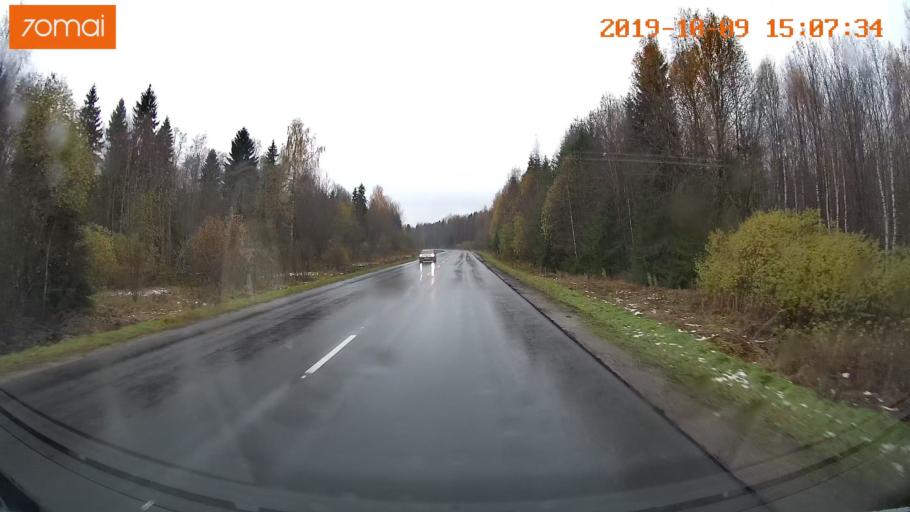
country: RU
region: Kostroma
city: Susanino
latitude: 58.2176
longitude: 41.6489
